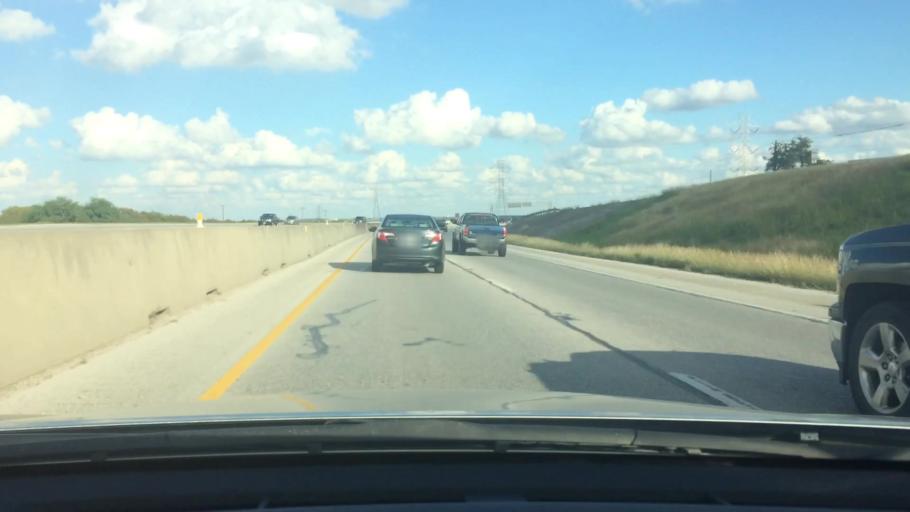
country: US
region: Texas
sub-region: Bexar County
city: Live Oak
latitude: 29.6028
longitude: -98.3638
